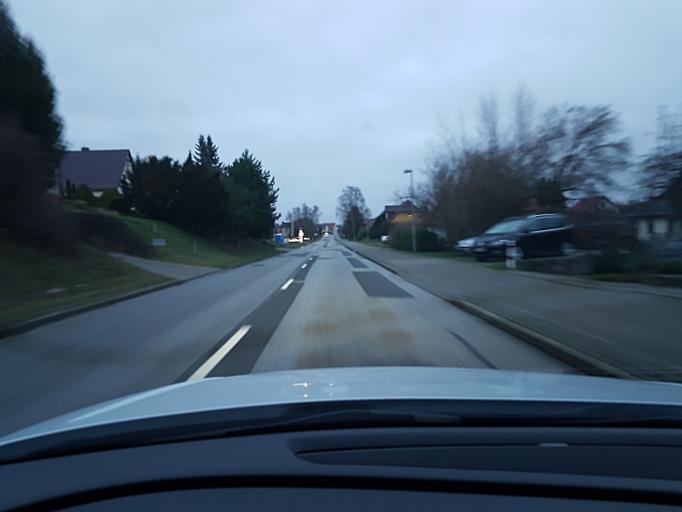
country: DE
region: Mecklenburg-Vorpommern
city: Satow-Oberhagen
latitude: 53.9834
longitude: 11.8796
